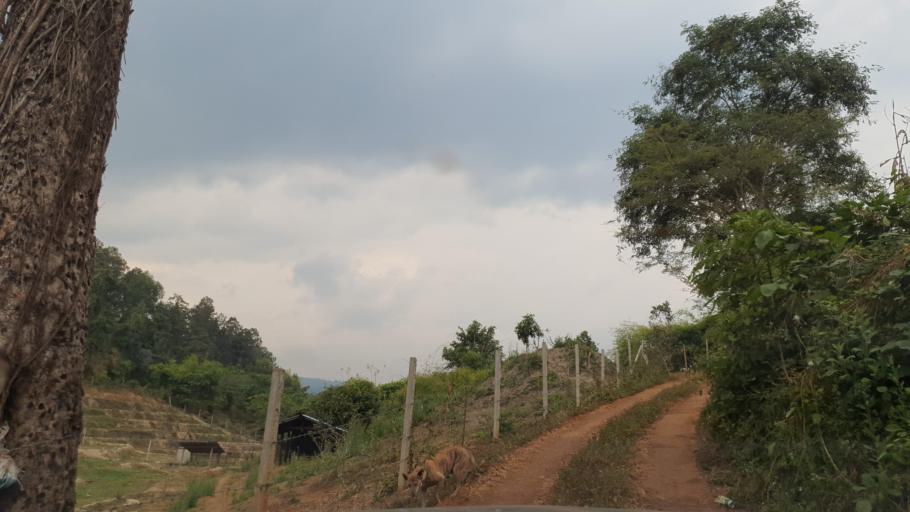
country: TH
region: Chiang Mai
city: Mae Wang
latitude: 18.6558
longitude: 98.6514
